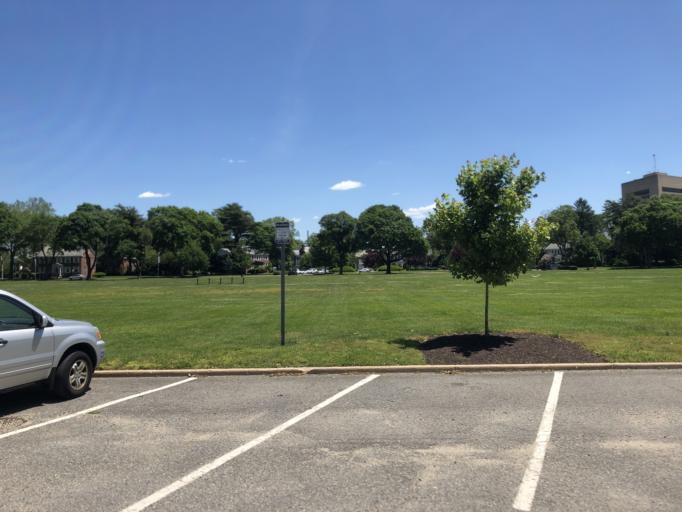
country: US
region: New York
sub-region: Nassau County
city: East Garden City
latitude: 40.7305
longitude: -73.5967
